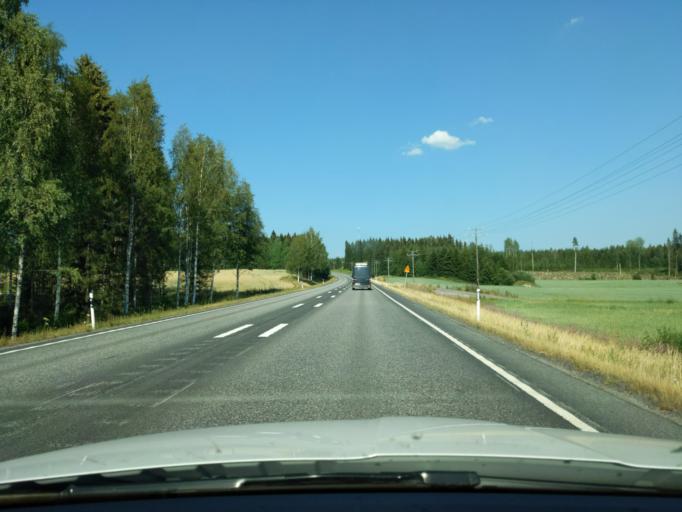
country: FI
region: Paijanne Tavastia
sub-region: Lahti
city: Jaervelae
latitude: 60.9284
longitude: 25.3744
